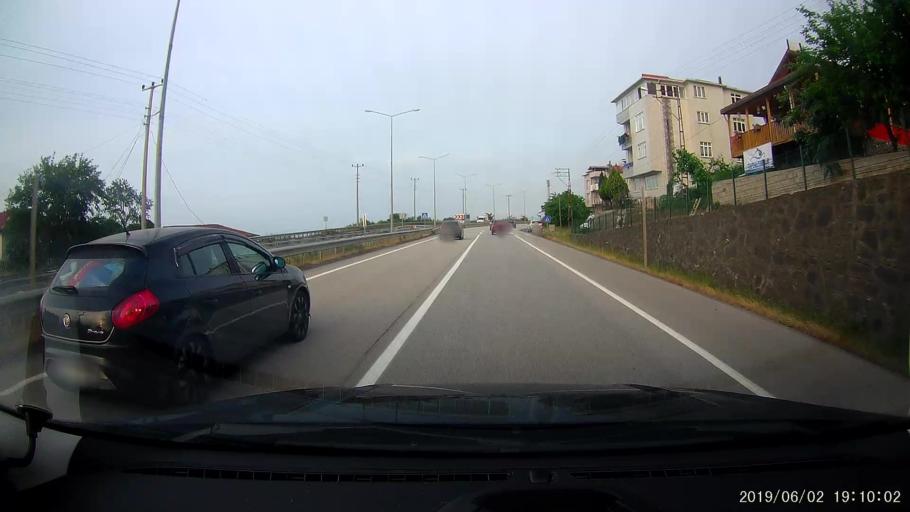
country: TR
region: Ordu
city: Gulyali
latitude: 40.9716
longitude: 38.0385
